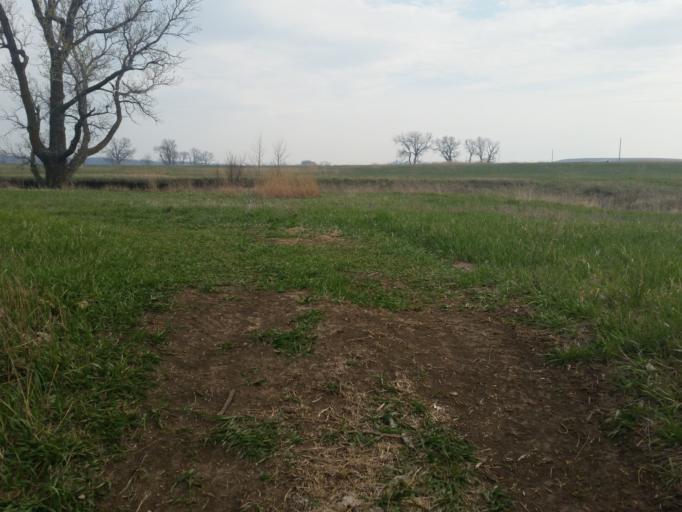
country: US
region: Kansas
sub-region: Chase County
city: Cottonwood Falls
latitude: 38.4295
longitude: -96.5557
